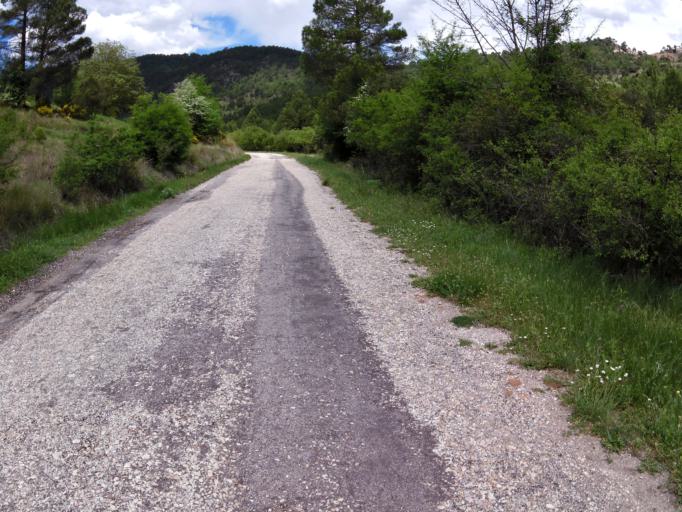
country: ES
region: Castille-La Mancha
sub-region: Provincia de Albacete
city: Paterna del Madera
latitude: 38.5779
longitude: -2.3404
